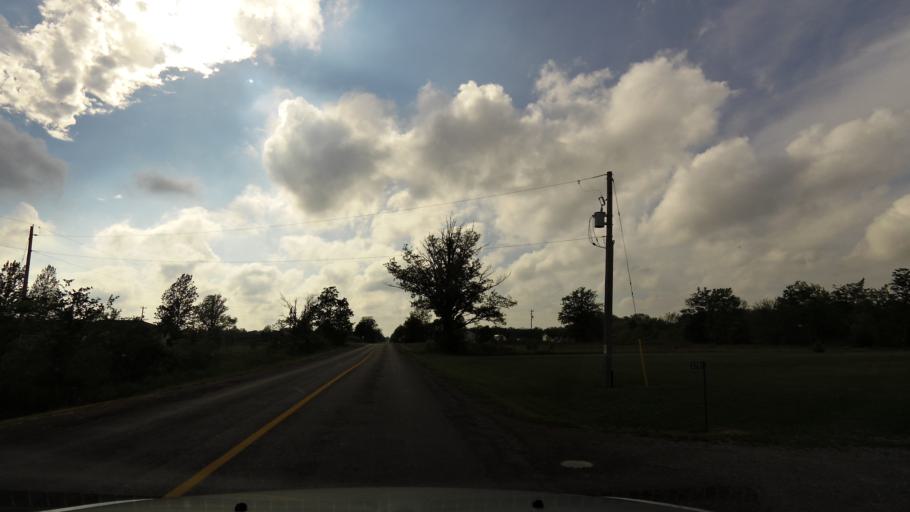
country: CA
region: Ontario
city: Brantford
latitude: 43.0149
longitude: -80.0842
